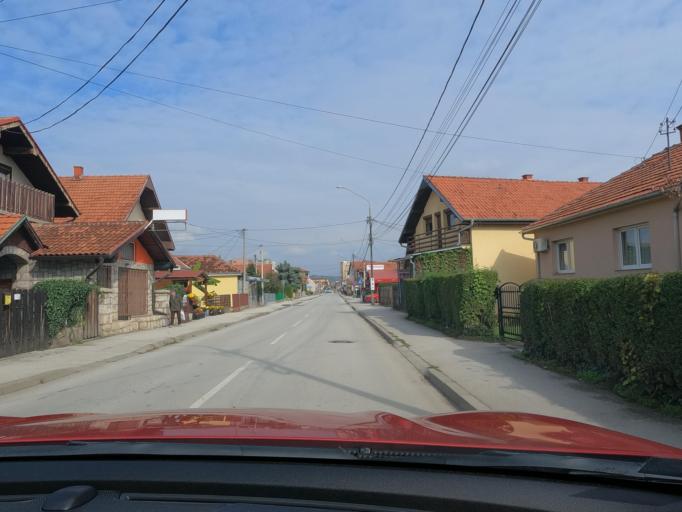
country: RS
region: Central Serbia
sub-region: Moravicki Okrug
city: Cacak
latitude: 43.8817
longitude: 20.3398
